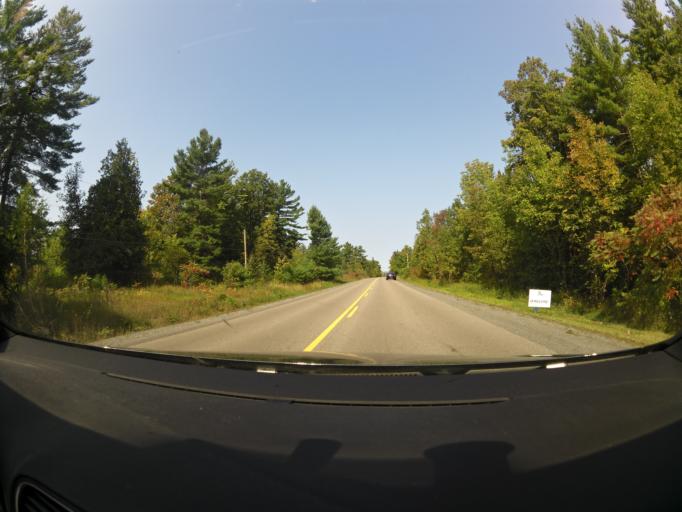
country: CA
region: Ontario
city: Arnprior
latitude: 45.4448
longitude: -76.1857
